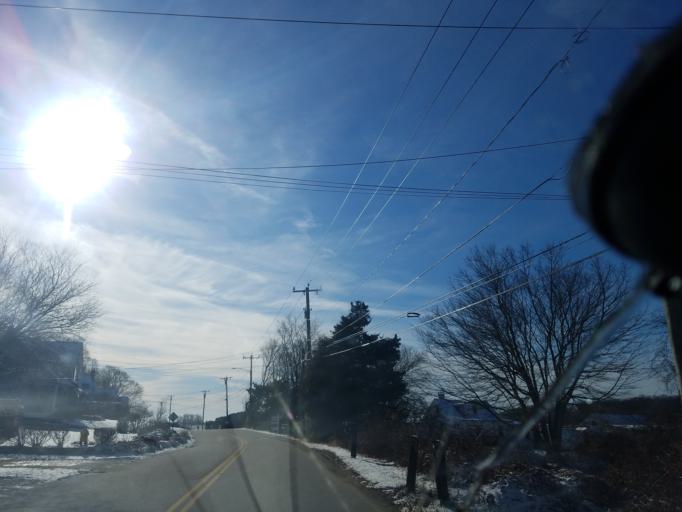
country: US
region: Connecticut
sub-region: New London County
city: Niantic
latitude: 41.3082
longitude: -72.2174
